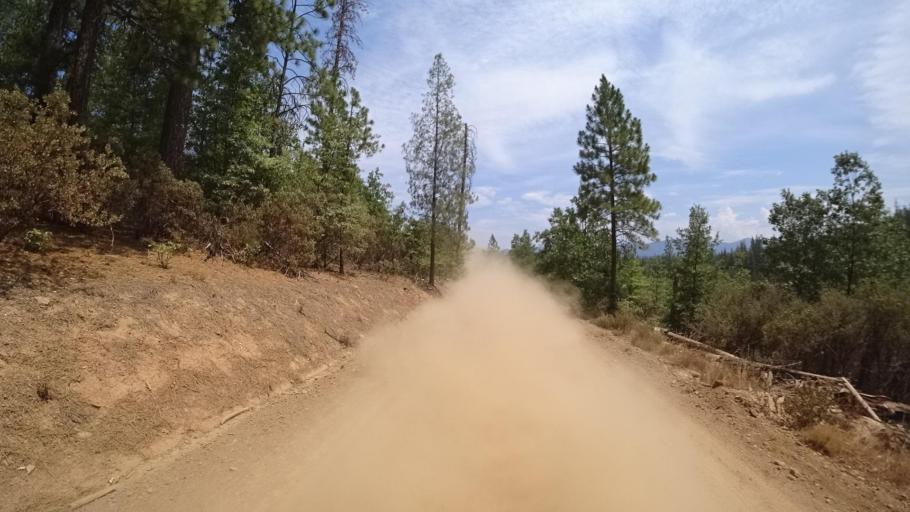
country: US
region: California
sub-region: Mariposa County
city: Midpines
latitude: 37.7423
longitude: -120.0754
